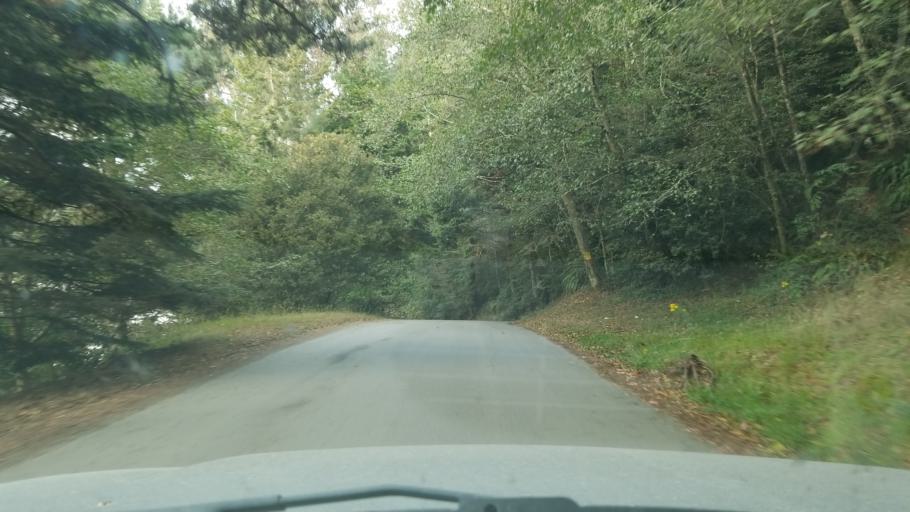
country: US
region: California
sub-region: Mendocino County
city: Fort Bragg
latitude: 39.4286
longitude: -123.7956
